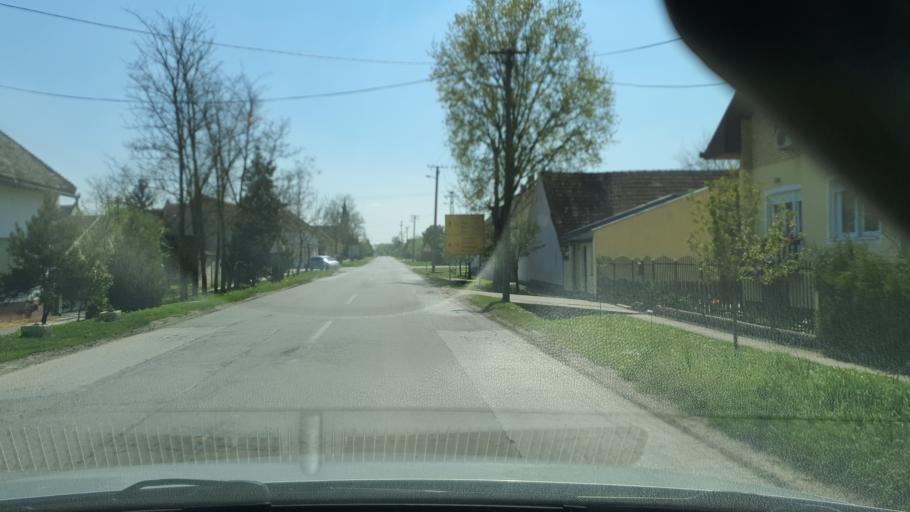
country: RS
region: Autonomna Pokrajina Vojvodina
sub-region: Zapadnobacki Okrug
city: Odzaci
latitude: 45.4565
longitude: 19.3311
